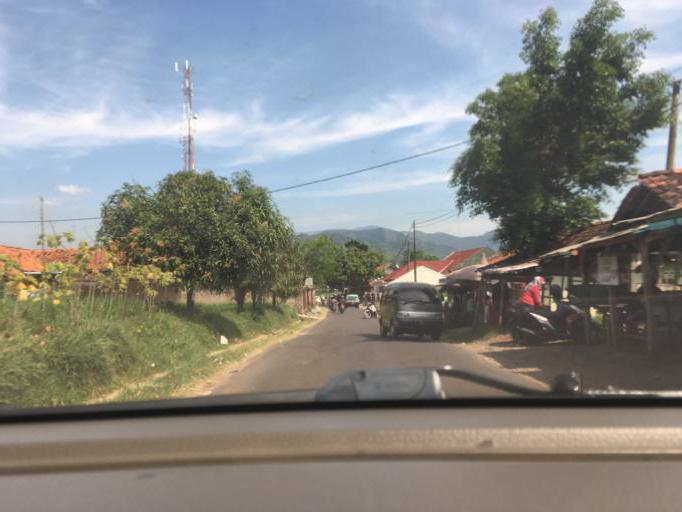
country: ID
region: West Java
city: Cilengkrang
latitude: -6.9458
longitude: 108.0961
